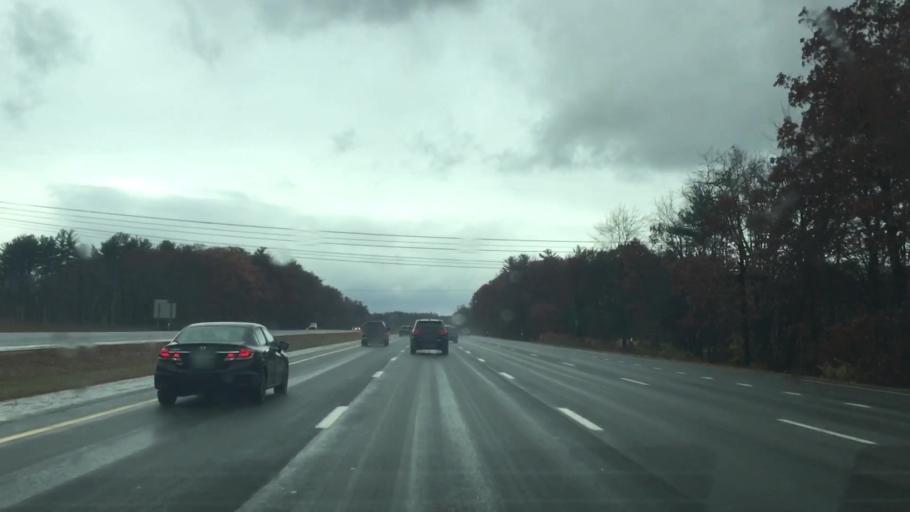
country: US
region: New Hampshire
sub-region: Rockingham County
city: Seabrook
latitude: 42.8975
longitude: -70.8791
